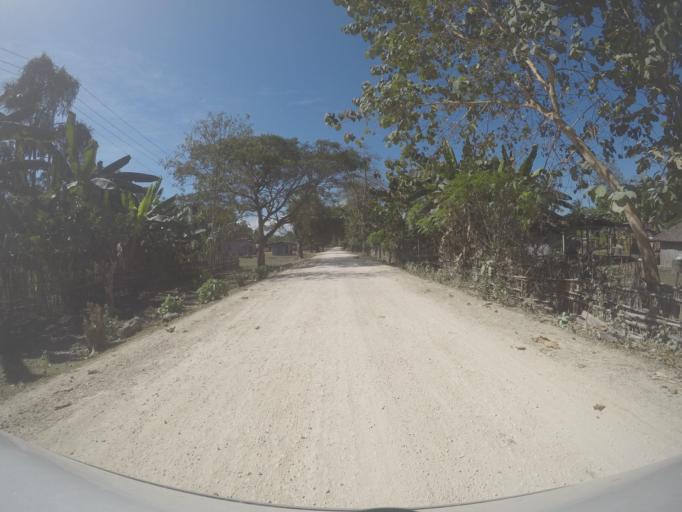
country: TL
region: Viqueque
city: Viqueque
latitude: -8.9018
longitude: 126.5061
